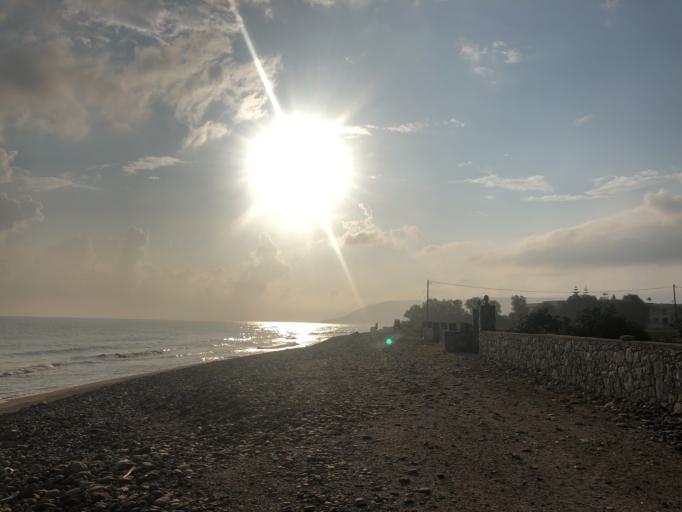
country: GR
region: Crete
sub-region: Nomos Chanias
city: Georgioupolis
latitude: 35.3529
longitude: 24.3076
